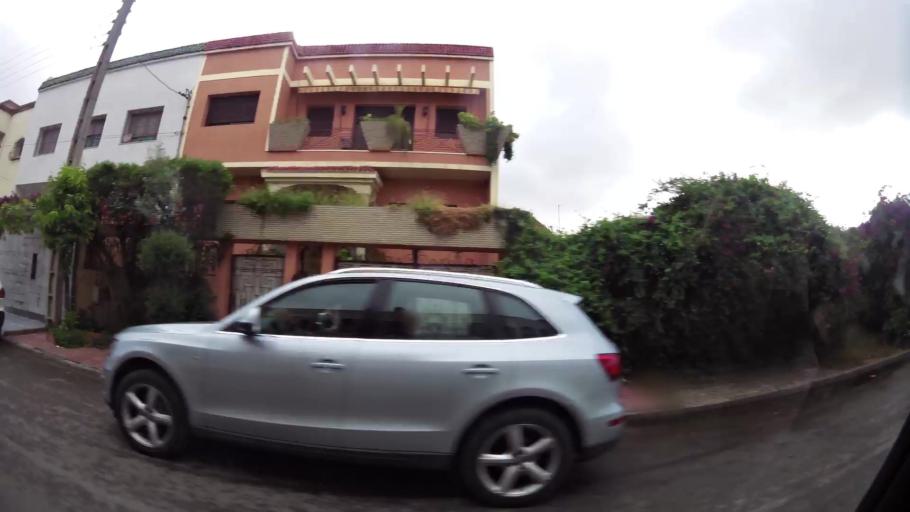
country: MA
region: Grand Casablanca
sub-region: Casablanca
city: Casablanca
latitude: 33.5620
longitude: -7.6779
